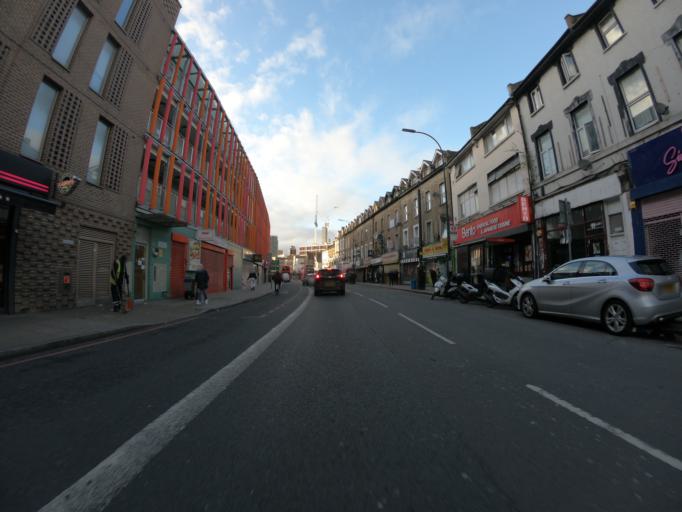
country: GB
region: England
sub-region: Greater London
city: Blackheath
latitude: 51.4617
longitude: -0.0070
